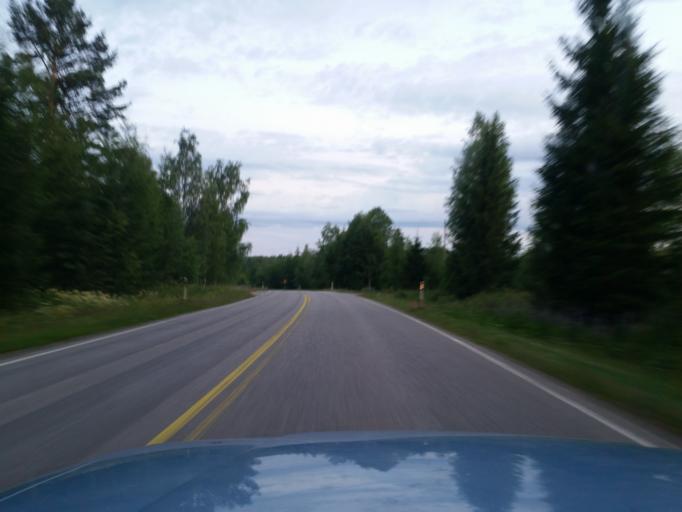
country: FI
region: Southern Savonia
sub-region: Savonlinna
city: Sulkava
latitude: 61.8274
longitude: 28.4410
